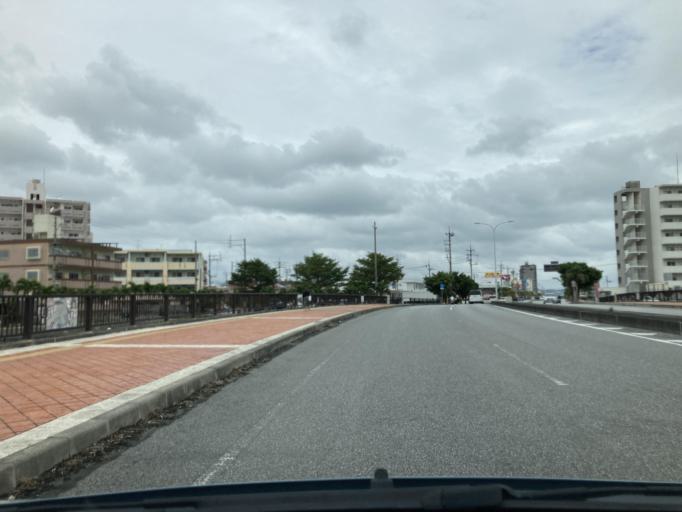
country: JP
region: Okinawa
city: Ginowan
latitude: 26.2024
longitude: 127.7604
